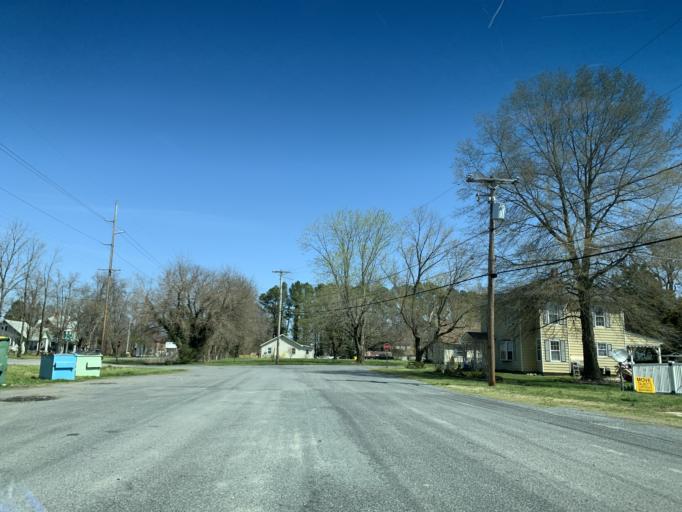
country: US
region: Maryland
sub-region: Talbot County
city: Easton
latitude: 38.8757
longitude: -75.9952
